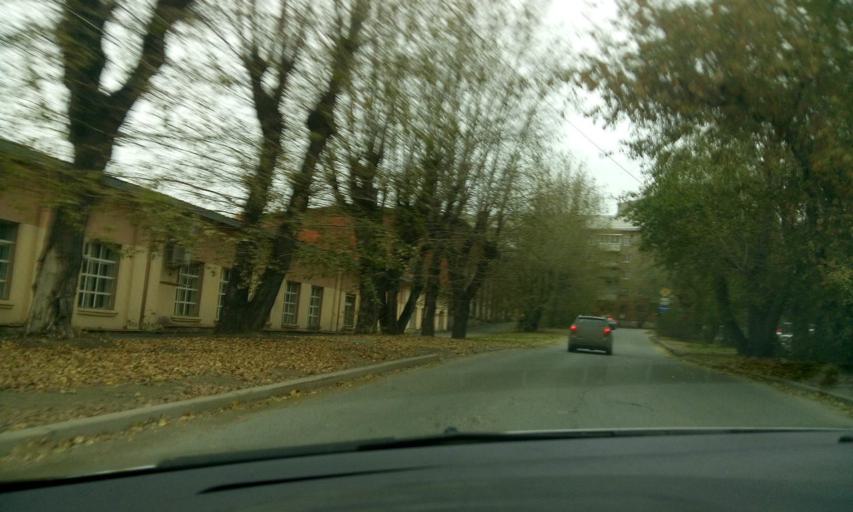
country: RU
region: Sverdlovsk
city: Yekaterinburg
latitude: 56.8598
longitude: 60.6277
